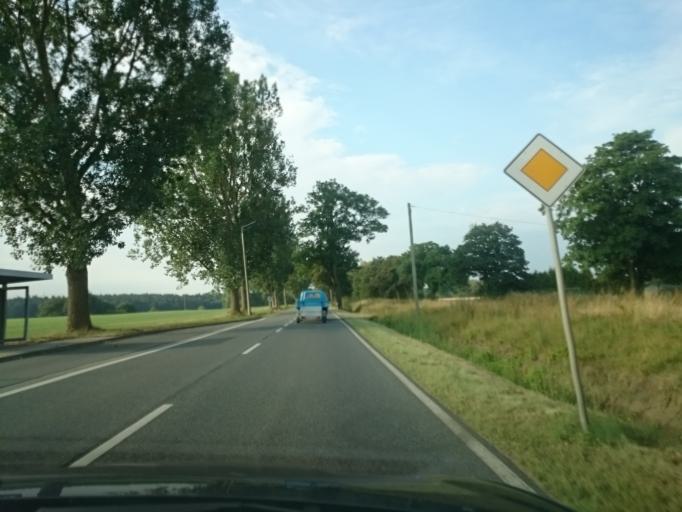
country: DE
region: Mecklenburg-Vorpommern
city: Demmin
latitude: 53.8733
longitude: 13.0187
